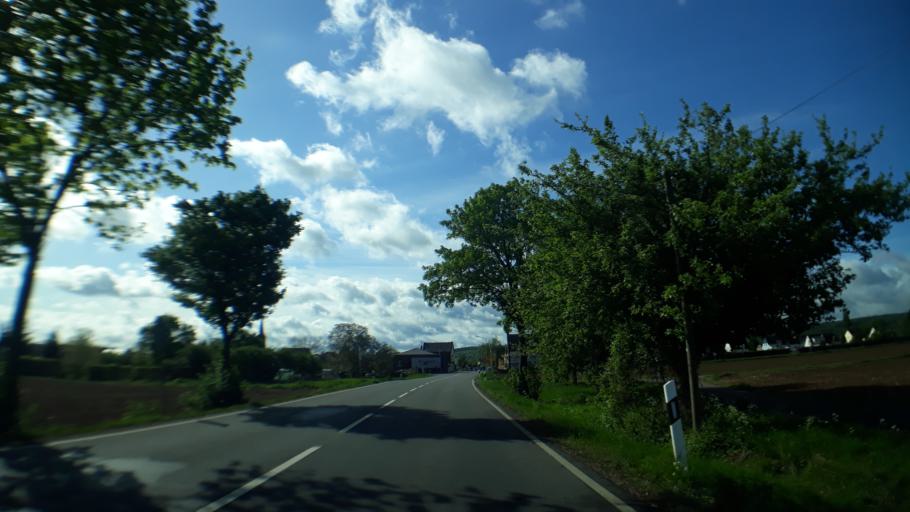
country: DE
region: North Rhine-Westphalia
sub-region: Regierungsbezirk Koln
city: Euskirchen
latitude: 50.6557
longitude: 6.7474
